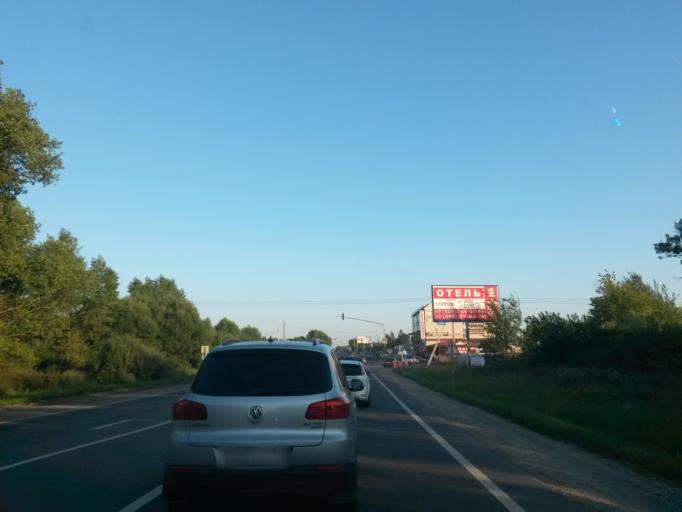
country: RU
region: Moskovskaya
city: Belyye Stolby
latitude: 55.3159
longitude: 37.8105
